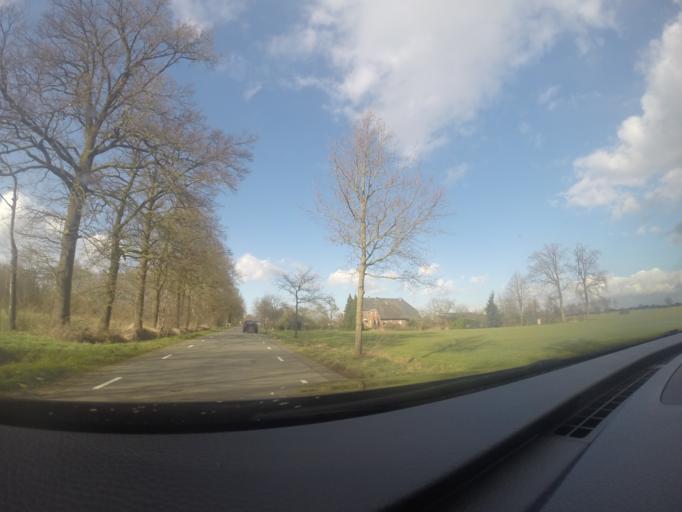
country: NL
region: Gelderland
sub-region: Oude IJsselstreek
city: Varsseveld
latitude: 52.0214
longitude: 6.4581
